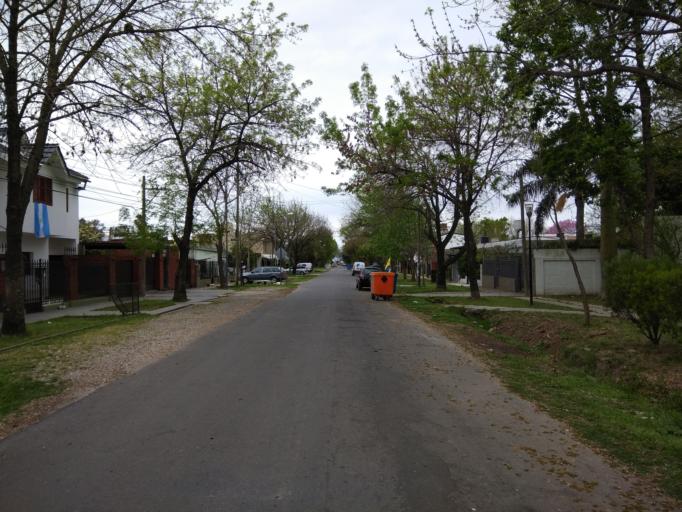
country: AR
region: Santa Fe
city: Granadero Baigorria
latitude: -32.8488
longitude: -60.7011
